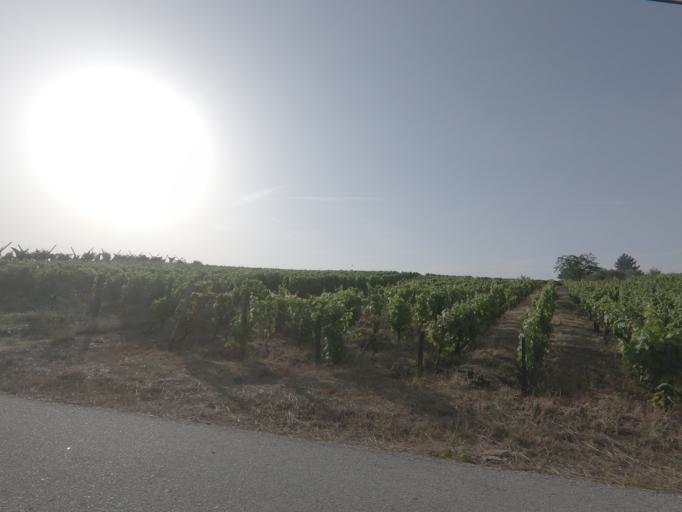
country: PT
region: Viseu
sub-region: Sao Joao da Pesqueira
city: Sao Joao da Pesqueira
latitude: 41.2391
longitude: -7.4685
